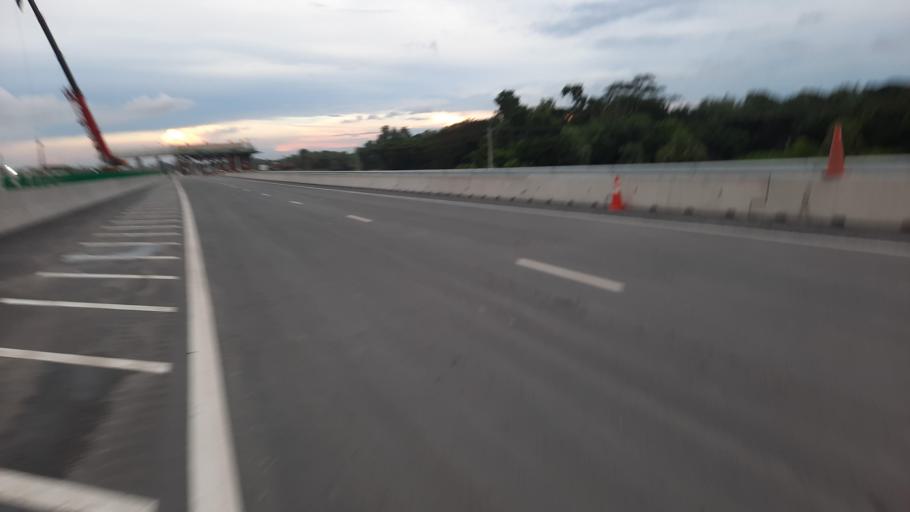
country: BD
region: Khulna
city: Kalia
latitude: 23.1906
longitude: 89.7021
